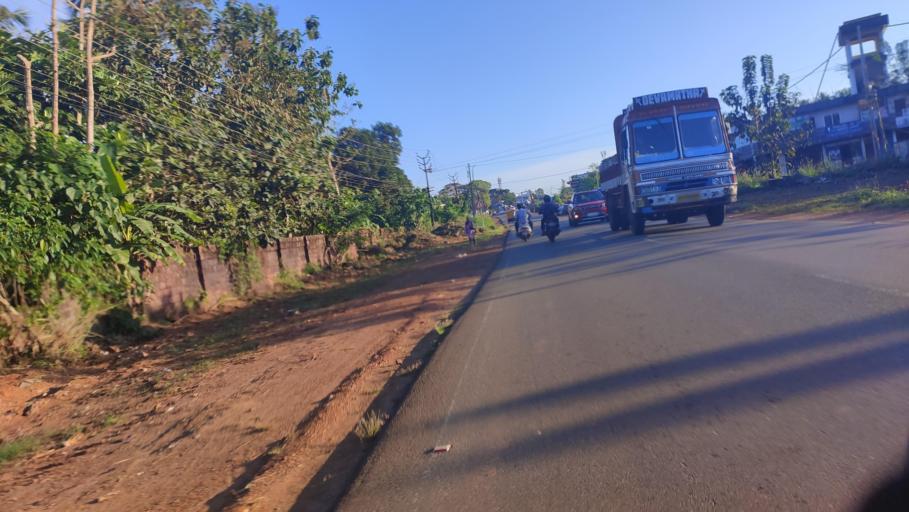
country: IN
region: Kerala
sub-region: Kasaragod District
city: Kasaragod
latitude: 12.4831
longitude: 75.0572
